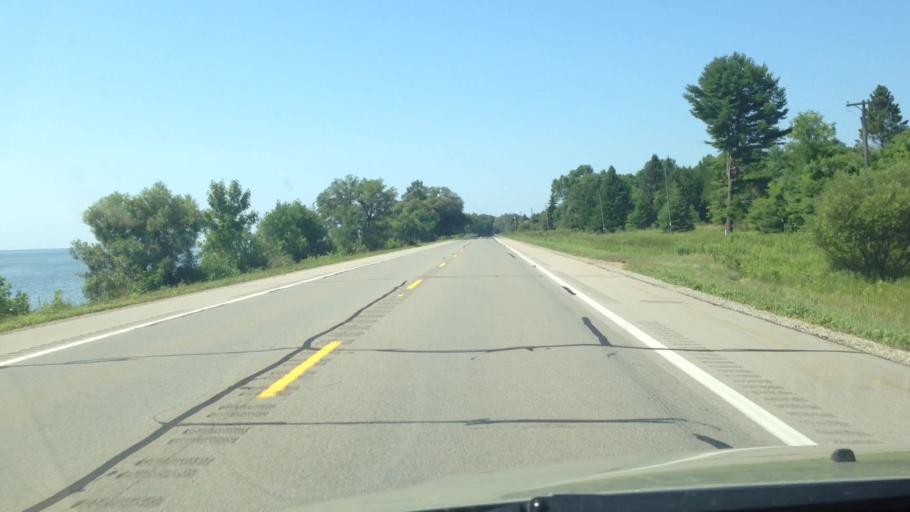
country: US
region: Michigan
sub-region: Menominee County
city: Menominee
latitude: 45.2505
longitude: -87.4876
